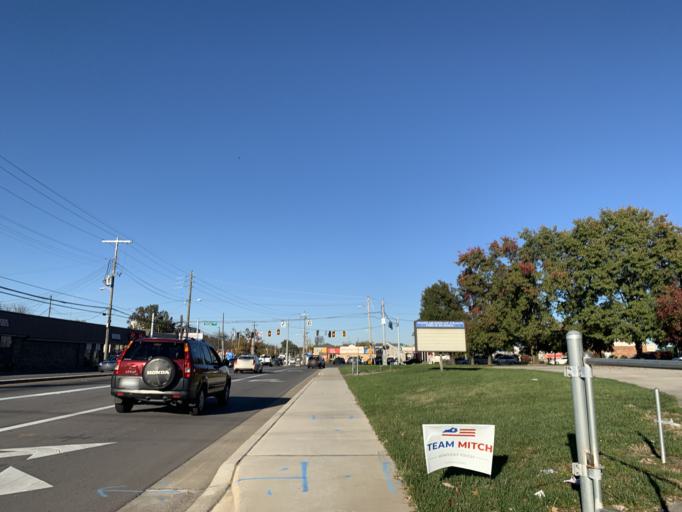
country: US
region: Kentucky
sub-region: Jefferson County
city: Shively
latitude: 38.1914
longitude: -85.8085
